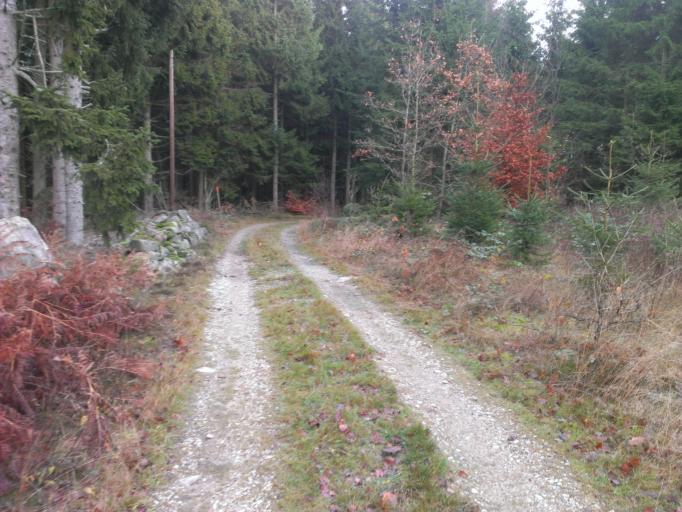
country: SE
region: Blekinge
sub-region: Karlskrona Kommun
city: Jaemjoe
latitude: 56.2558
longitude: 15.8860
